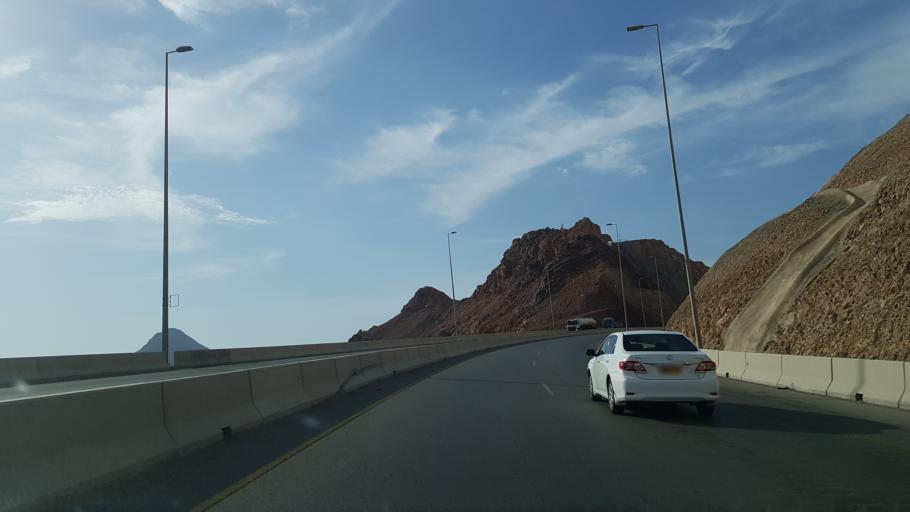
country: OM
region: Muhafazat ad Dakhiliyah
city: Bidbid
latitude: 23.4546
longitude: 58.1176
